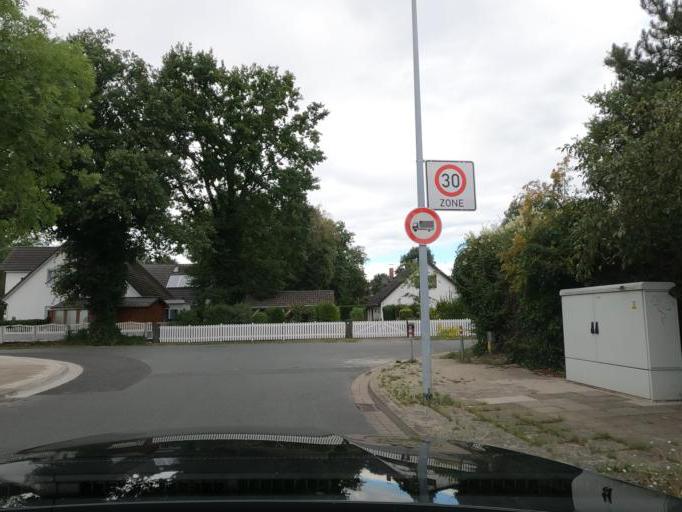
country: DE
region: Lower Saxony
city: Isernhagen Farster Bauerschaft
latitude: 52.4216
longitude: 9.8243
